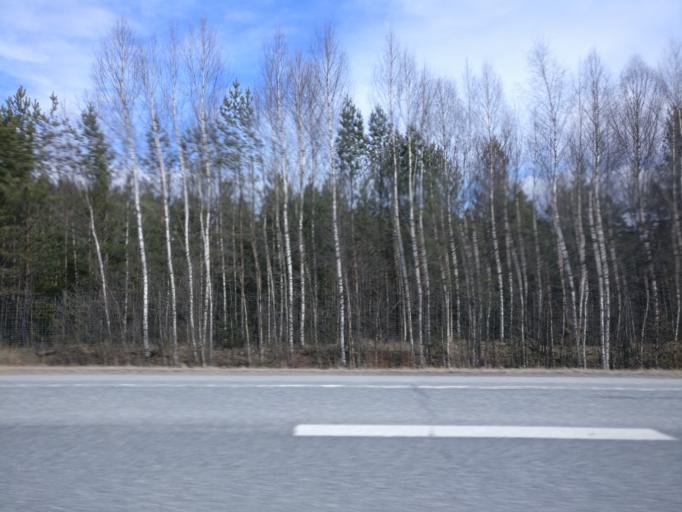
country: FI
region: Haeme
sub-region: Haemeenlinna
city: Janakkala
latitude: 60.9238
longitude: 24.5258
